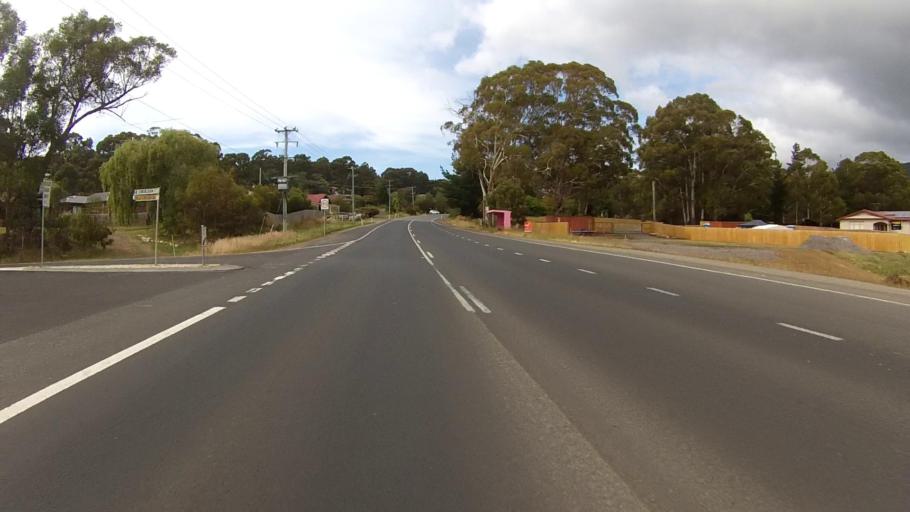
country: AU
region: Tasmania
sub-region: Kingborough
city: Margate
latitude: -43.0740
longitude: 147.2567
